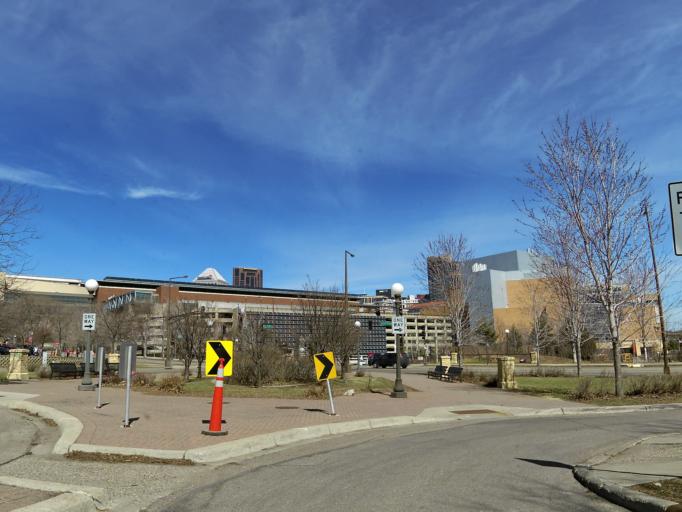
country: US
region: Minnesota
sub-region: Ramsey County
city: Saint Paul
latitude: 44.9417
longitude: -93.1017
